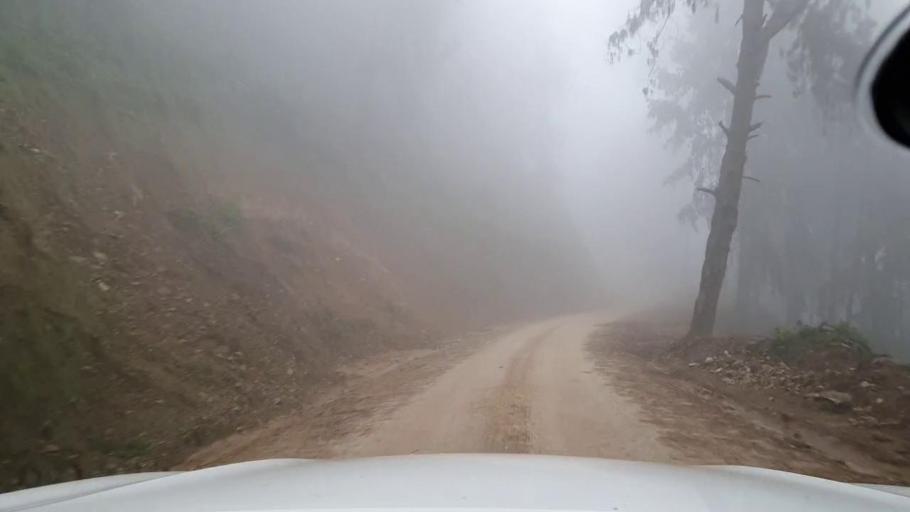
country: BI
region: Cibitoke
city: Cibitoke
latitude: -2.5936
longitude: 29.1947
